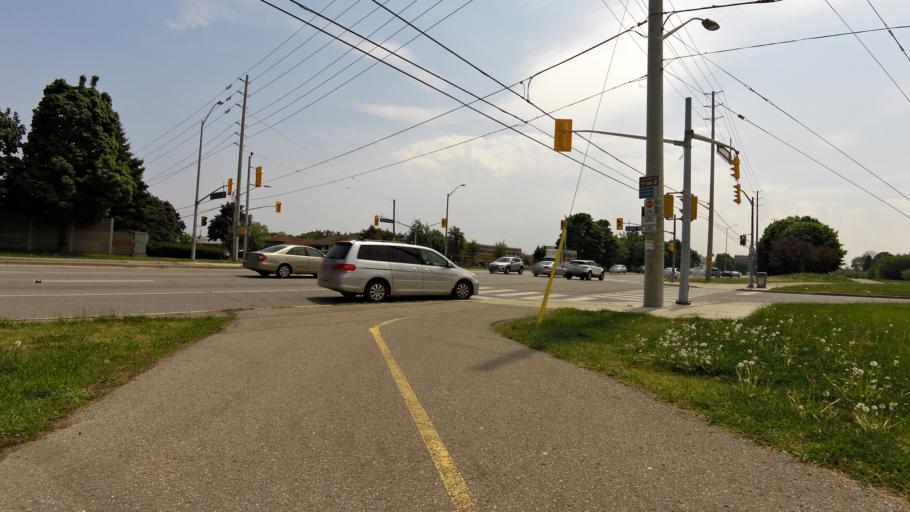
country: CA
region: Ontario
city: Mississauga
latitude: 43.5816
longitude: -79.5994
